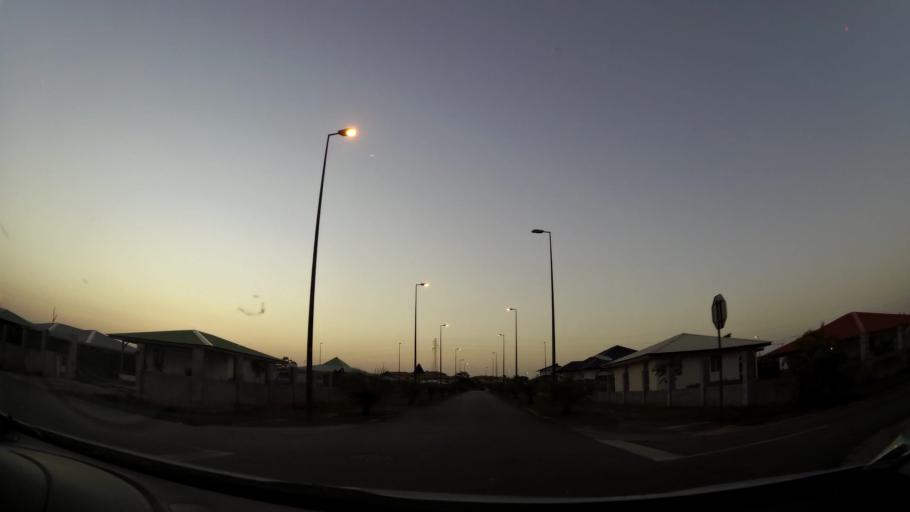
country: GF
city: Macouria
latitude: 4.9247
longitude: -52.4087
